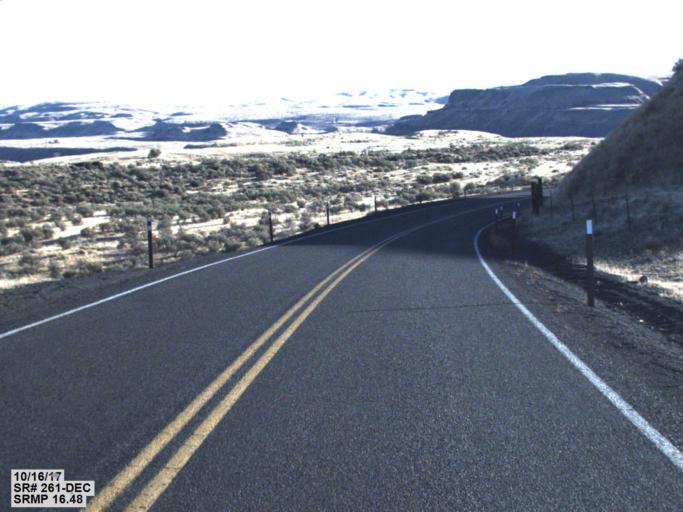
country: US
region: Washington
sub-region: Walla Walla County
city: Waitsburg
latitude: 46.6081
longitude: -118.2223
